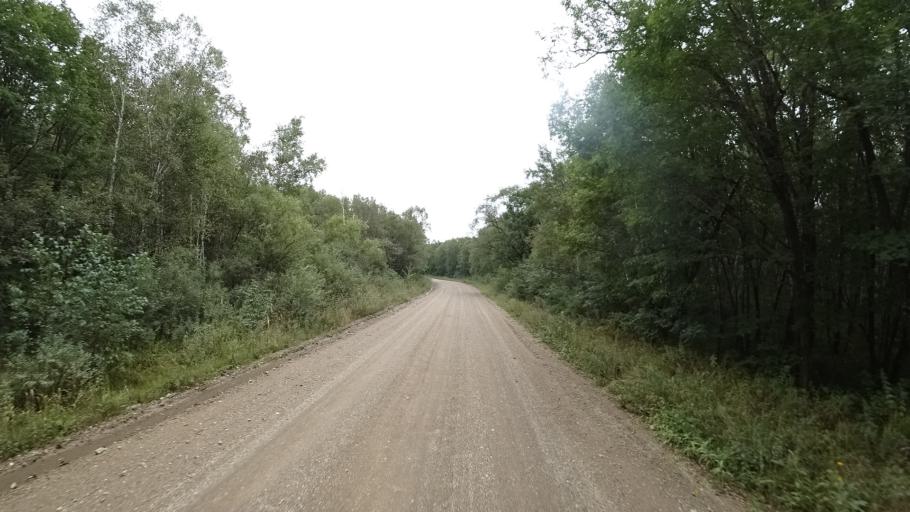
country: RU
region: Primorskiy
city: Ivanovka
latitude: 44.0407
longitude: 132.4957
